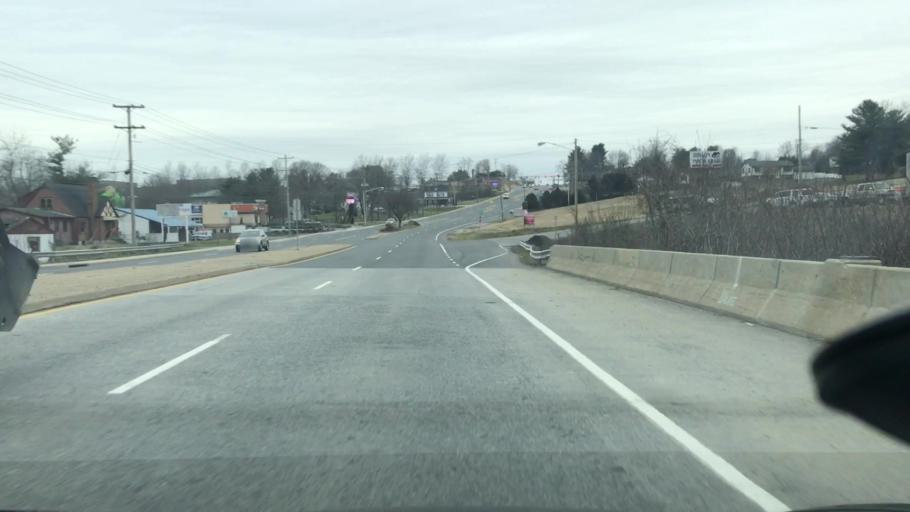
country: US
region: Virginia
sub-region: Montgomery County
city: Christiansburg
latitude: 37.1401
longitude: -80.4147
